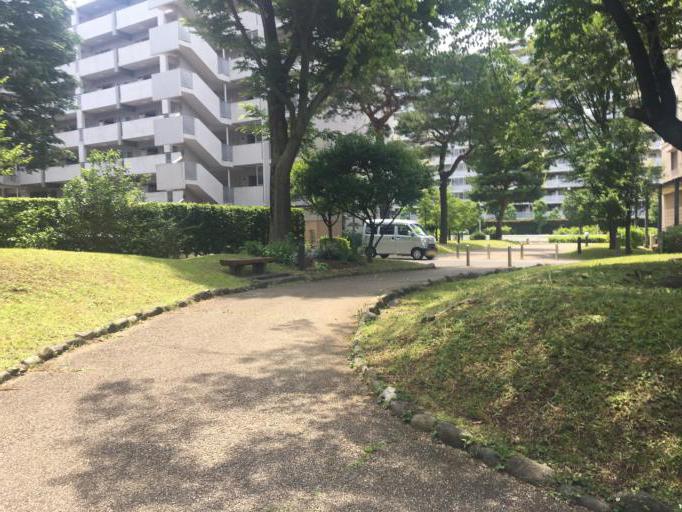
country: JP
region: Tokyo
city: Tanashicho
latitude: 35.7472
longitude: 139.5355
